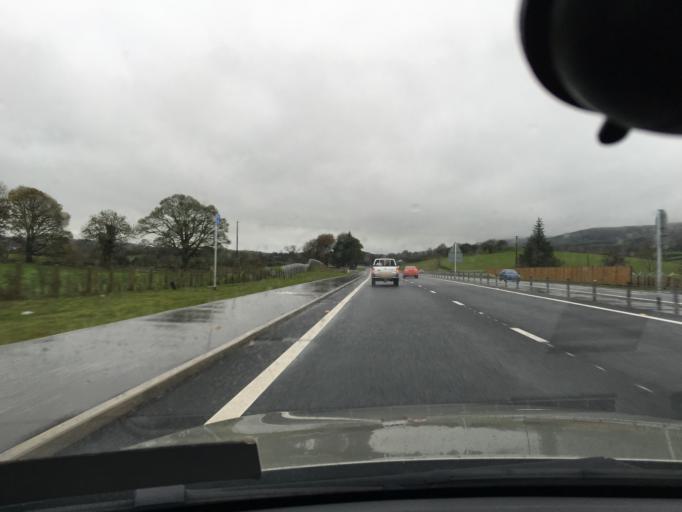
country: GB
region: Northern Ireland
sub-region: Larne District
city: Larne
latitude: 54.8298
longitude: -5.8788
